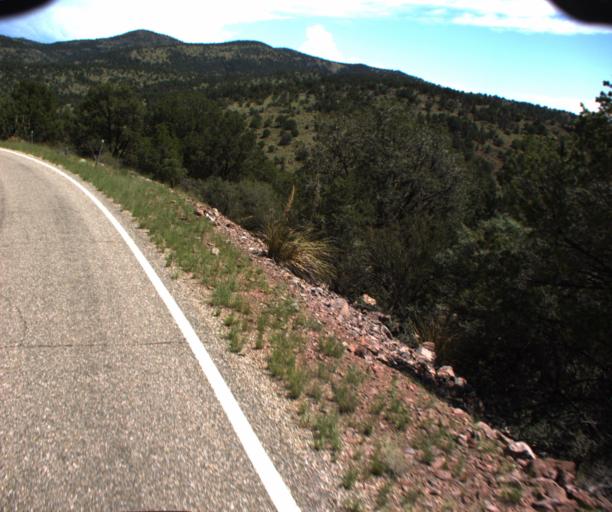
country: US
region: Arizona
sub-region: Greenlee County
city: Morenci
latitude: 33.3505
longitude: -109.3445
